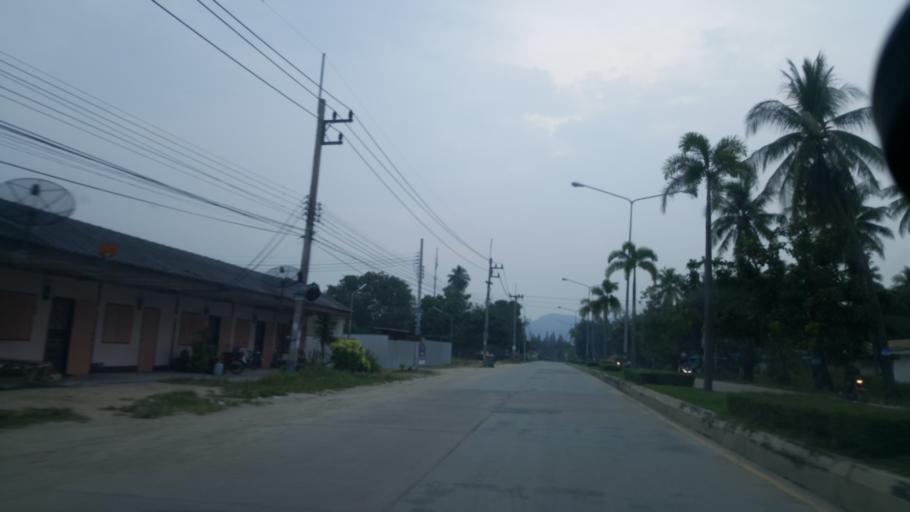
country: TH
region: Chon Buri
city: Si Racha
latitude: 13.2369
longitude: 101.0078
